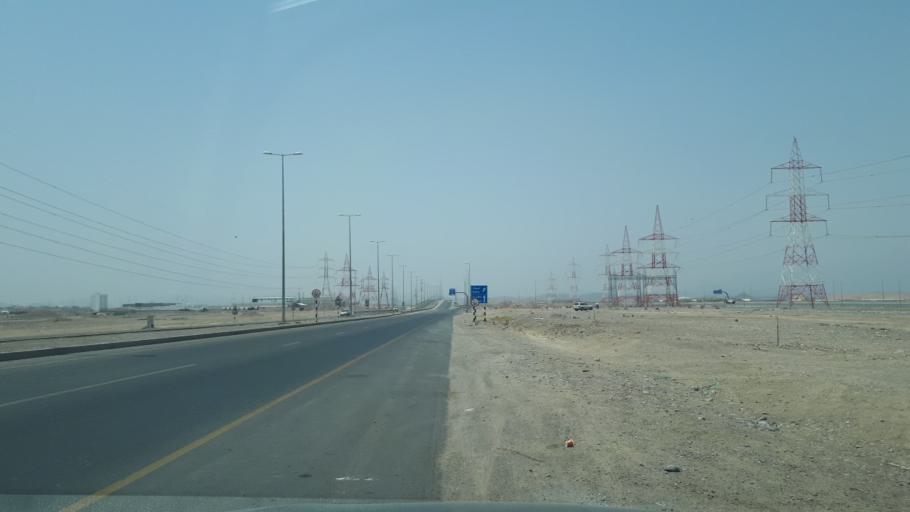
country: OM
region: Muhafazat Masqat
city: As Sib al Jadidah
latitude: 23.6159
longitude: 58.0912
